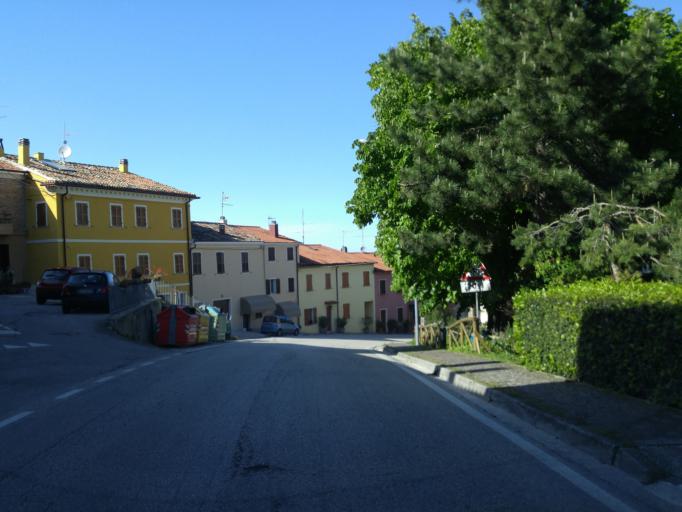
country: IT
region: The Marches
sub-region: Provincia di Pesaro e Urbino
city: Monteciccardo
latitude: 43.8300
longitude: 12.8172
